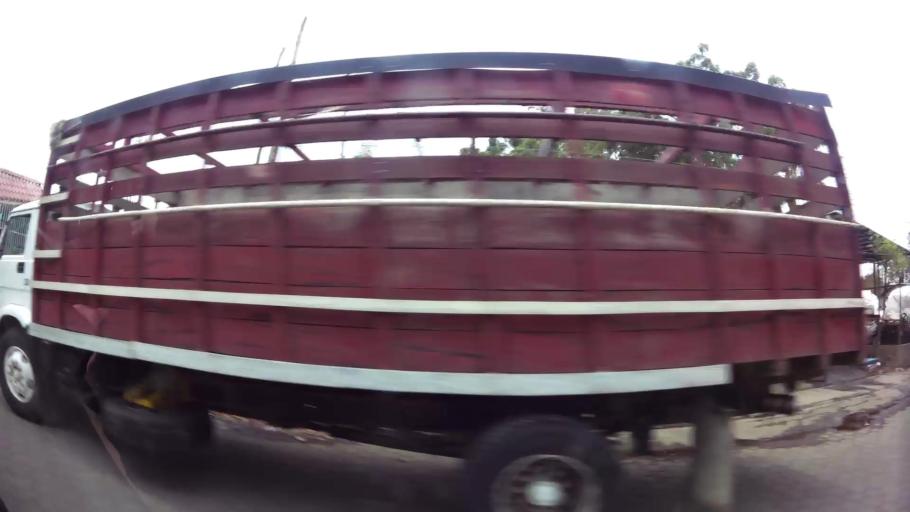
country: NI
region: Leon
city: Leon
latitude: 12.4213
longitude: -86.8775
